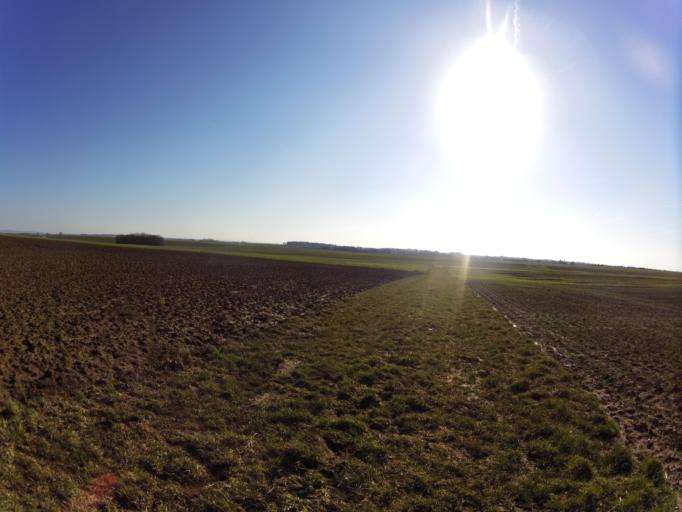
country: DE
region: Bavaria
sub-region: Regierungsbezirk Unterfranken
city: Giebelstadt
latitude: 49.6822
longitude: 9.9697
